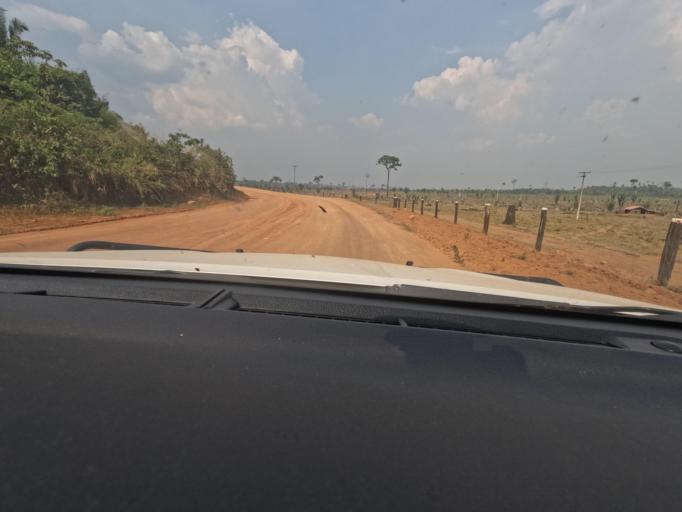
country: BR
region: Rondonia
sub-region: Porto Velho
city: Porto Velho
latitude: -8.6842
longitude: -63.1681
